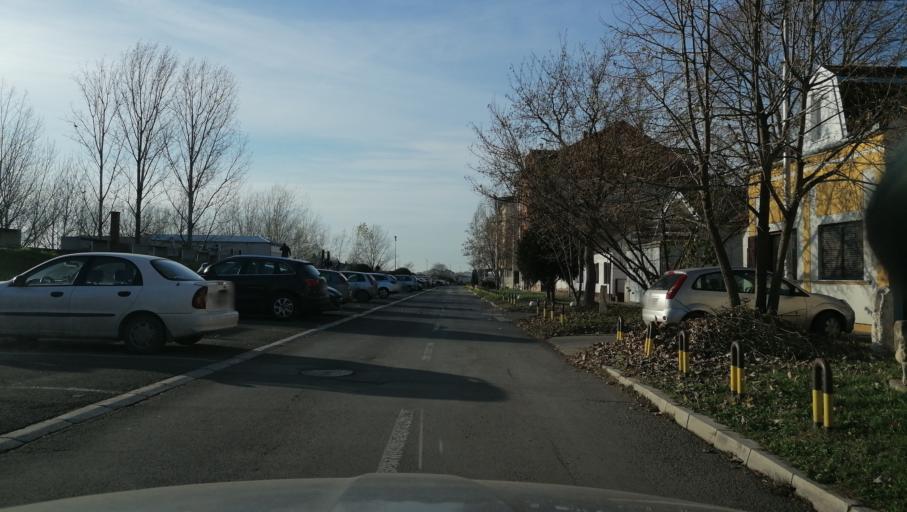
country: RS
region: Autonomna Pokrajina Vojvodina
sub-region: Sremski Okrug
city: Sremska Mitrovica
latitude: 44.9626
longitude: 19.6128
